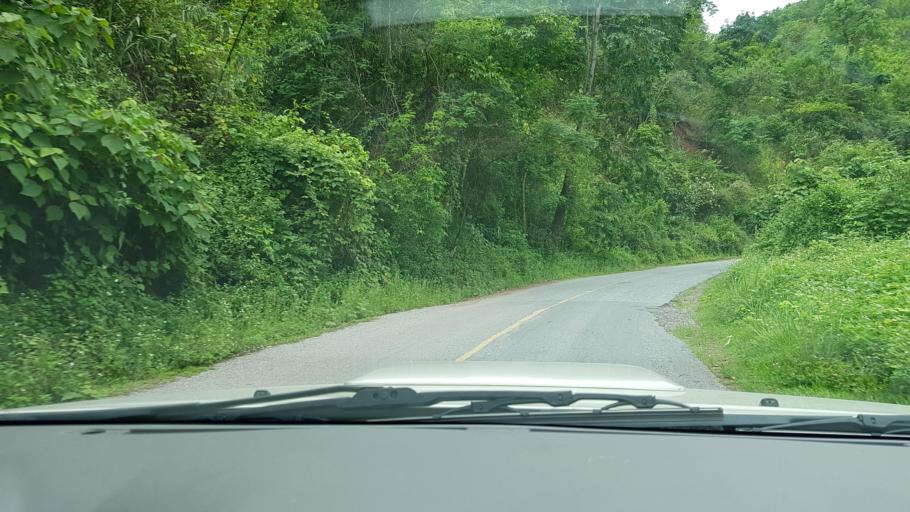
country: LA
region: Loungnamtha
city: Muang Nale
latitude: 20.3683
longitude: 101.7189
